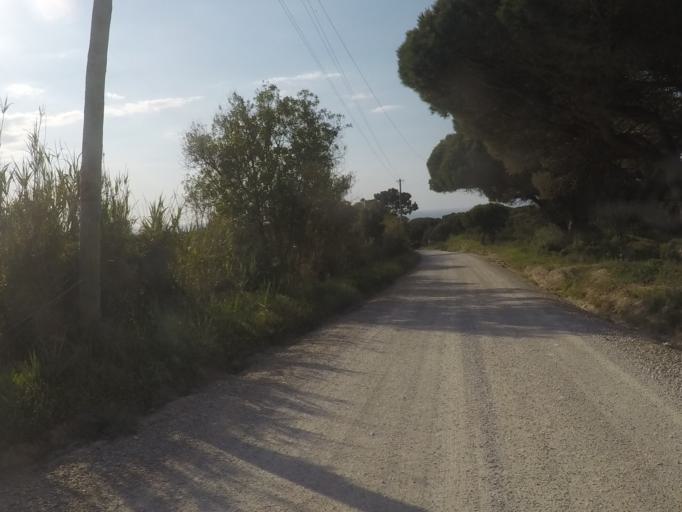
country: PT
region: Setubal
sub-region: Sesimbra
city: Sesimbra
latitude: 38.4375
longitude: -9.1891
